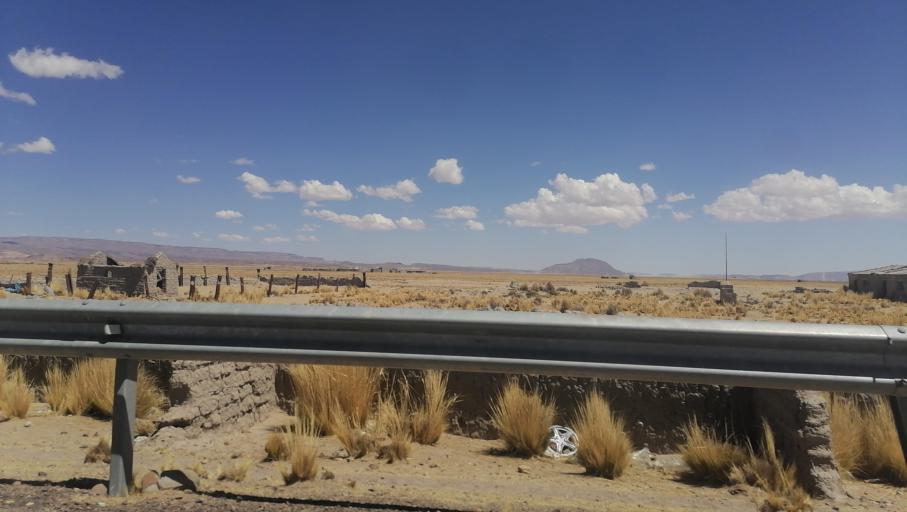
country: BO
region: Oruro
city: Challapata
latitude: -19.1725
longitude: -66.8046
